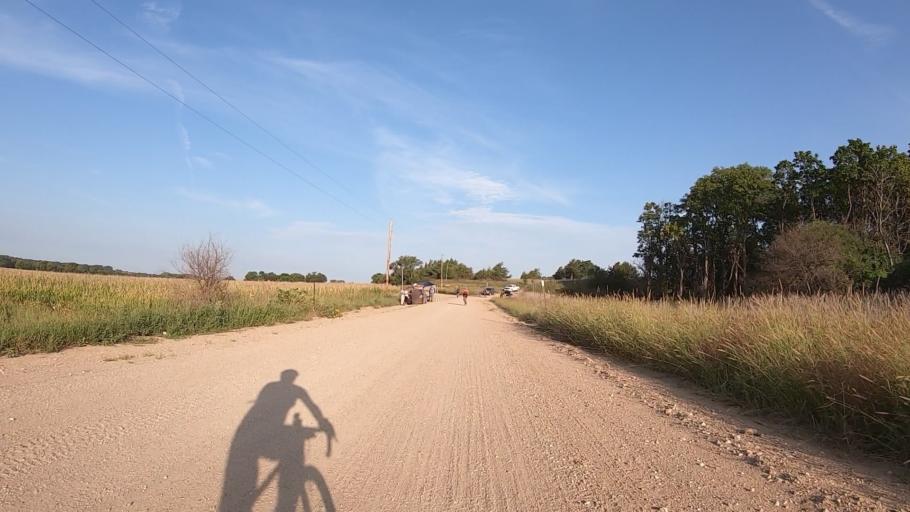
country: US
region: Kansas
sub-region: Marshall County
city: Blue Rapids
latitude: 39.7256
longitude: -96.7872
